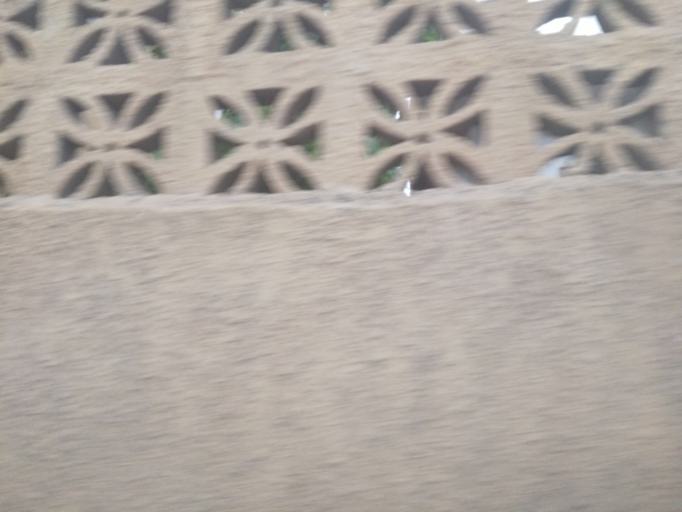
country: TZ
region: Dar es Salaam
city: Magomeni
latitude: -6.7878
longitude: 39.2722
